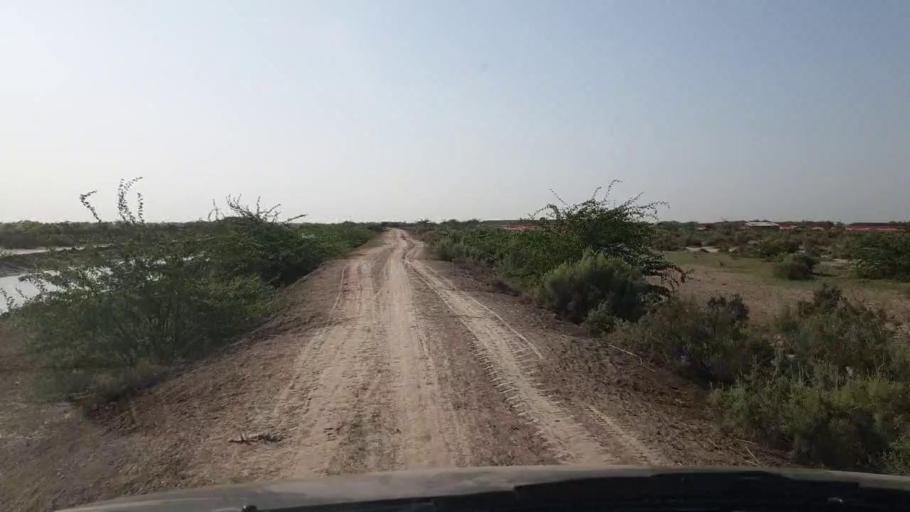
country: PK
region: Sindh
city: Kadhan
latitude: 24.6124
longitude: 69.0730
